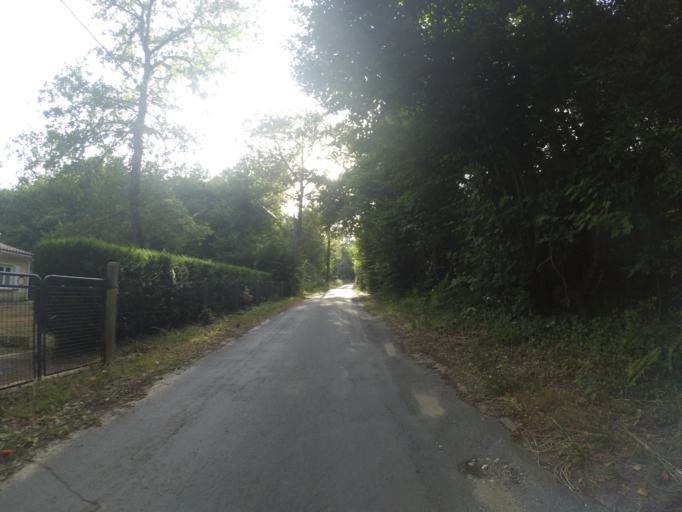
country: FR
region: Poitou-Charentes
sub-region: Departement de la Charente-Maritime
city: Meschers-sur-Gironde
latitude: 45.5789
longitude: -0.9757
